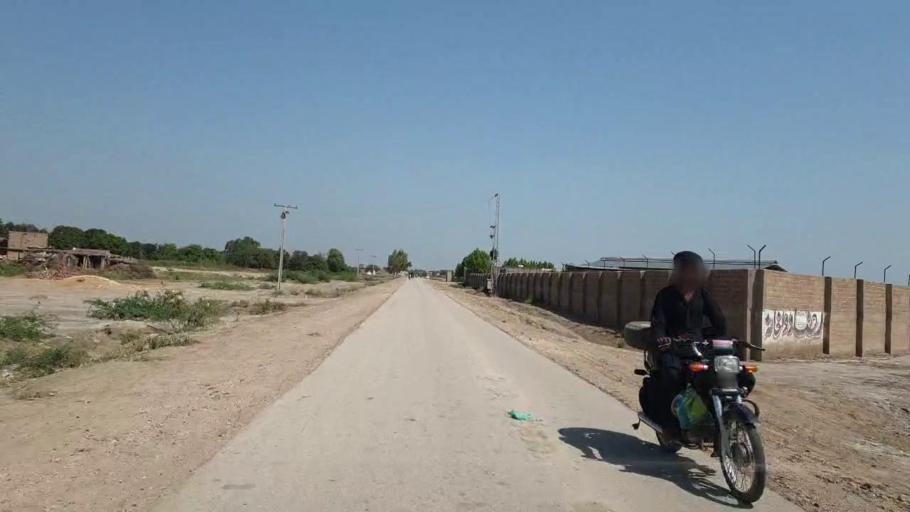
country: PK
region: Sindh
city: Hyderabad
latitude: 25.4439
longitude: 68.4097
